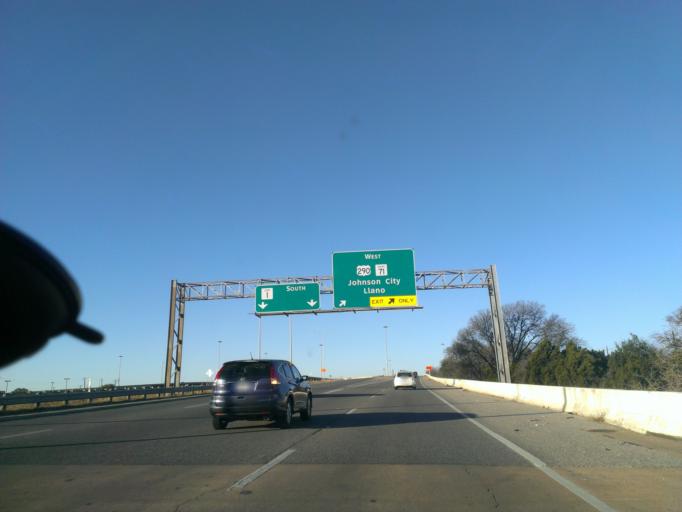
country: US
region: Texas
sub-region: Travis County
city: Rollingwood
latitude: 30.2388
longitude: -97.8199
